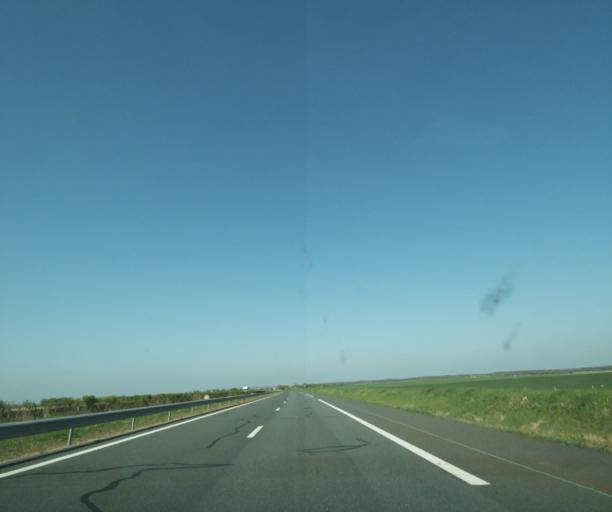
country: FR
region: Ile-de-France
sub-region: Departement de Seine-et-Marne
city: Chateau-Landon
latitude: 48.1007
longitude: 2.7015
